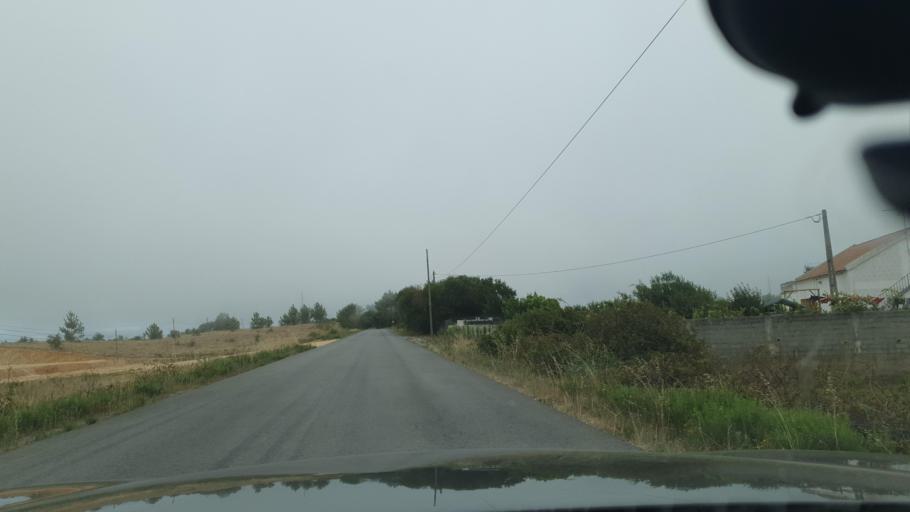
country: PT
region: Beja
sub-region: Odemira
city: Sao Teotonio
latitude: 37.5035
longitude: -8.6901
